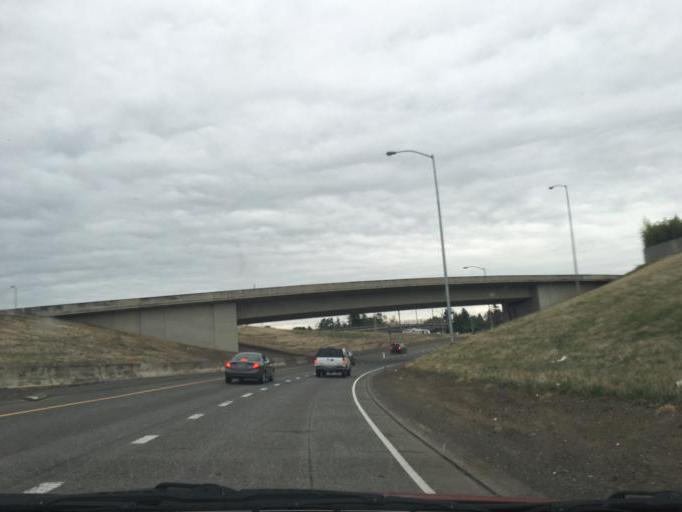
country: US
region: Oregon
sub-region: Multnomah County
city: Lents
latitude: 45.5308
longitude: -122.5669
